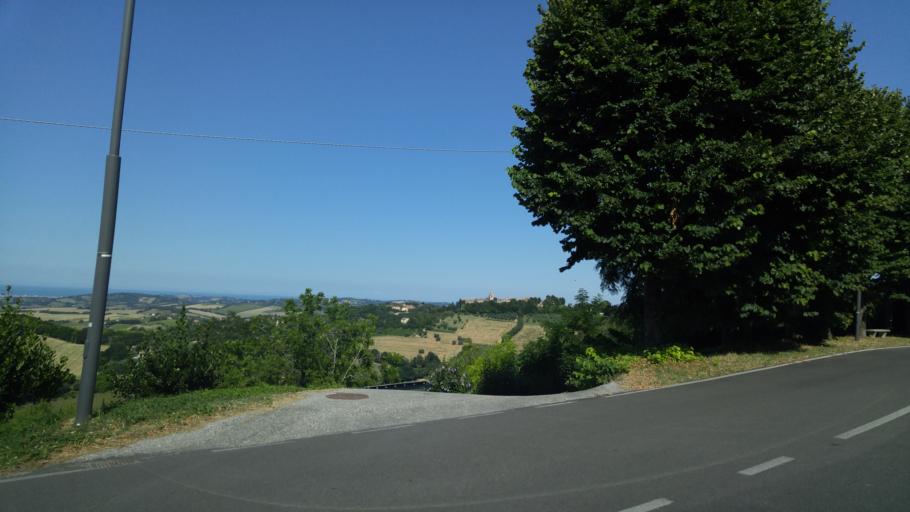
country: IT
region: The Marches
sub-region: Provincia di Pesaro e Urbino
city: Sant'Angelo in Lizzola
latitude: 43.8283
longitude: 12.8029
